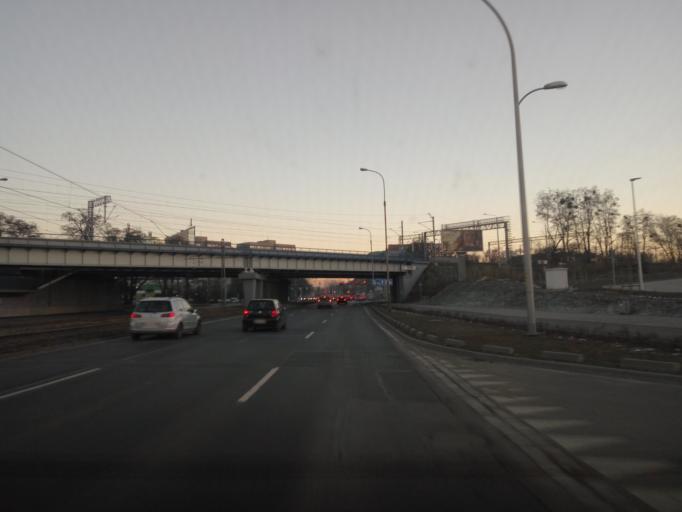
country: PL
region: Lower Silesian Voivodeship
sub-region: Powiat wroclawski
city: Wroclaw
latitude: 51.1187
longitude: 16.9980
